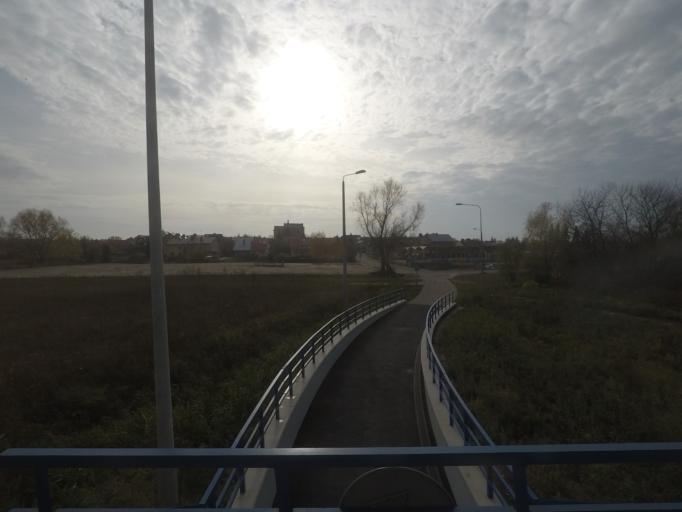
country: PL
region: Subcarpathian Voivodeship
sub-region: Powiat ropczycko-sedziszowski
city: Sedziszow Malopolski
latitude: 50.0749
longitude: 21.7020
